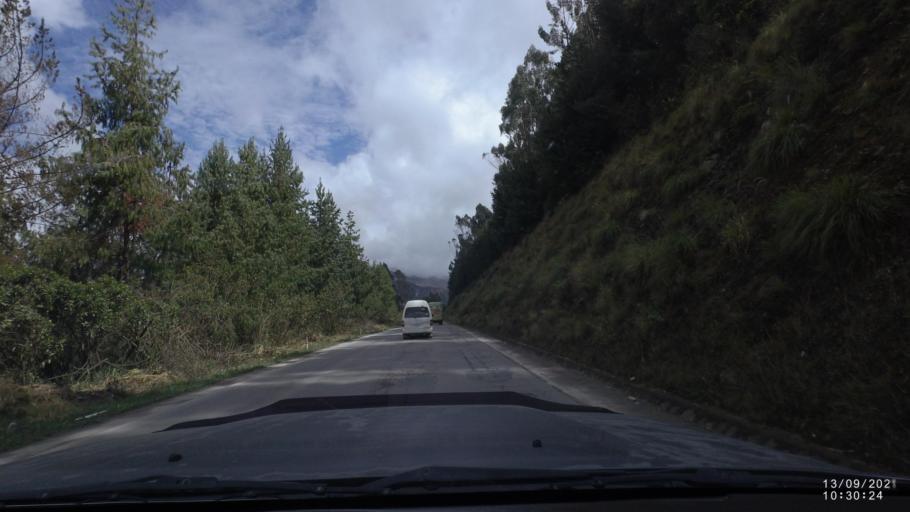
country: BO
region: Cochabamba
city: Colomi
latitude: -17.2625
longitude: -65.8866
